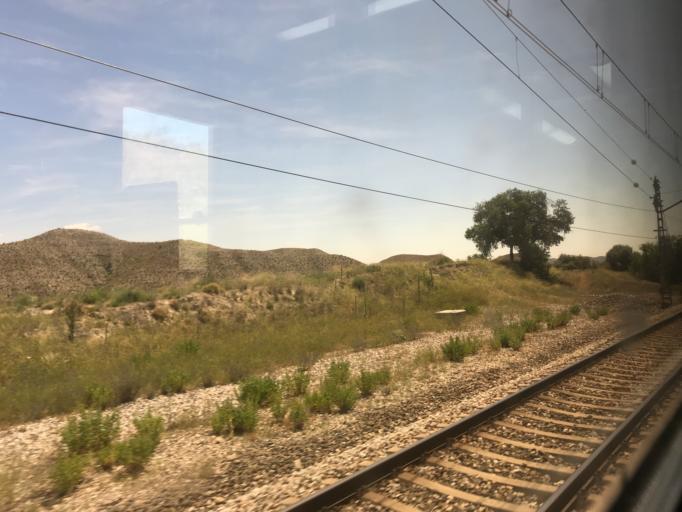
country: ES
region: Madrid
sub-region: Provincia de Madrid
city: Ciempozuelos
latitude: 40.1659
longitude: -3.6138
